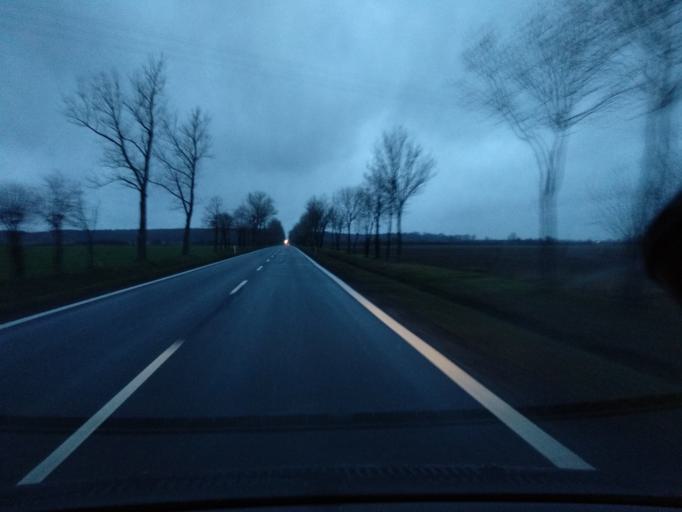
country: PL
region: Lower Silesian Voivodeship
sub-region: Powiat legnicki
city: Prochowice
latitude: 51.2382
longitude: 16.4167
